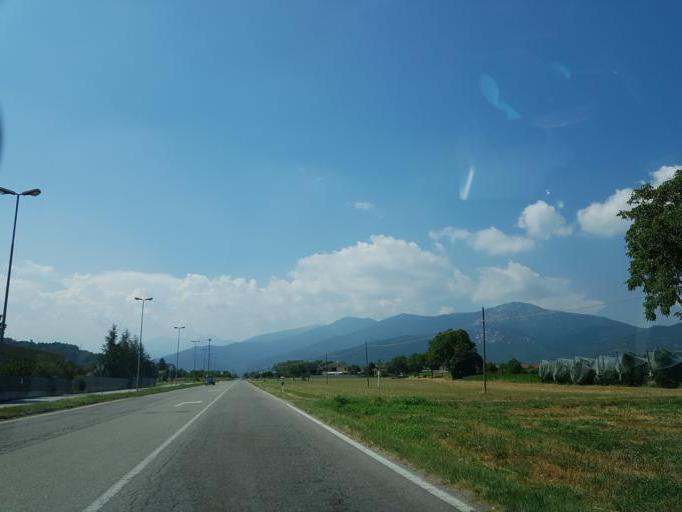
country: IT
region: Piedmont
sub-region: Provincia di Cuneo
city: Montemale di Cuneo
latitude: 44.4491
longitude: 7.3952
